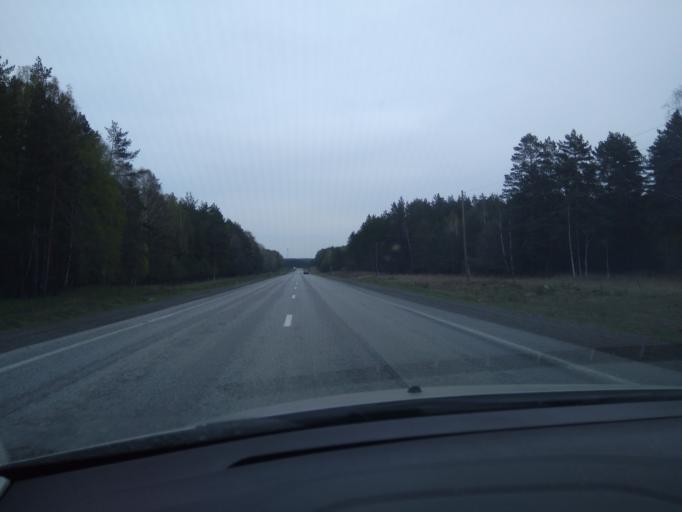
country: RU
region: Sverdlovsk
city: Gryaznovskoye
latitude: 56.7861
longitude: 61.6822
